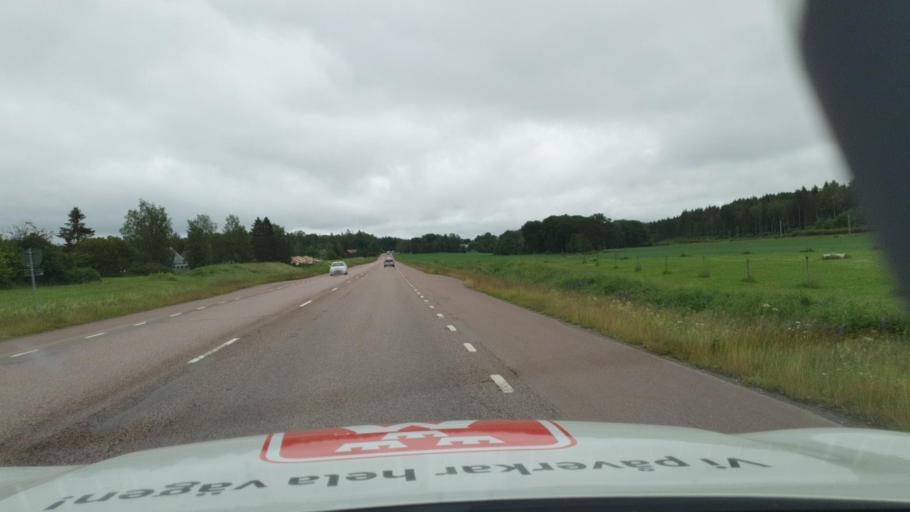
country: SE
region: Vaermland
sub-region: Grums Kommun
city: Grums
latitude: 59.3669
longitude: 13.1197
